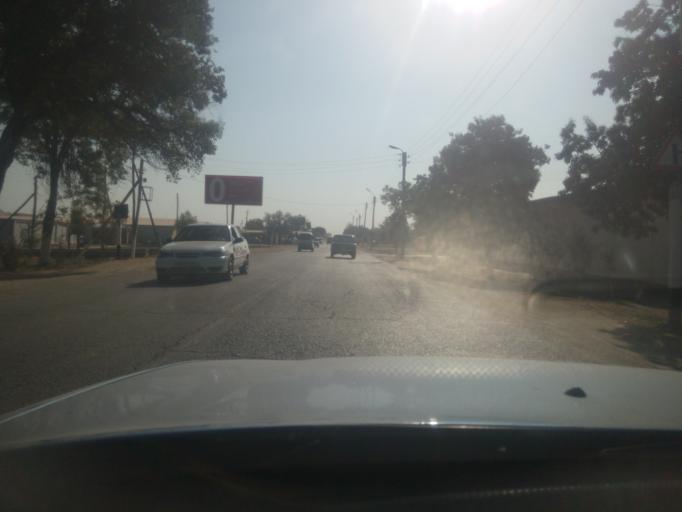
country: UZ
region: Sirdaryo
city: Guliston
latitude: 40.4945
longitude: 68.7959
